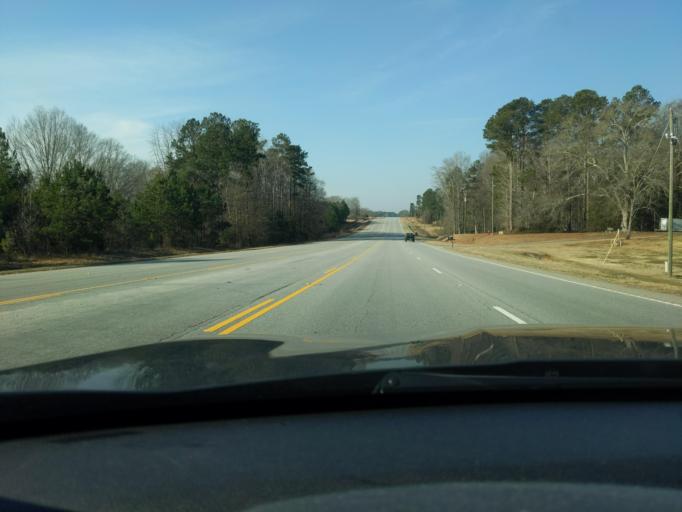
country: US
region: South Carolina
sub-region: Abbeville County
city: Abbeville
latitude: 34.1298
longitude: -82.4275
